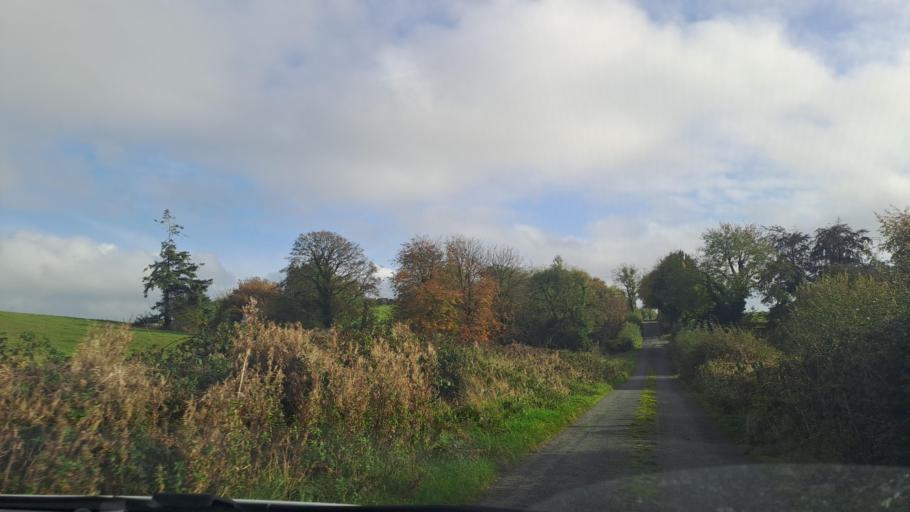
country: IE
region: Ulster
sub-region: County Monaghan
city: Carrickmacross
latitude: 54.0211
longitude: -6.7649
